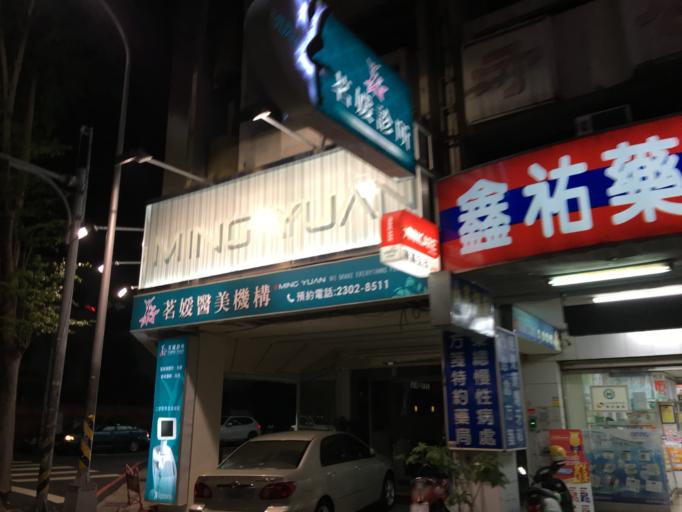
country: TW
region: Taiwan
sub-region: Taichung City
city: Taichung
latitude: 24.1477
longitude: 120.6699
